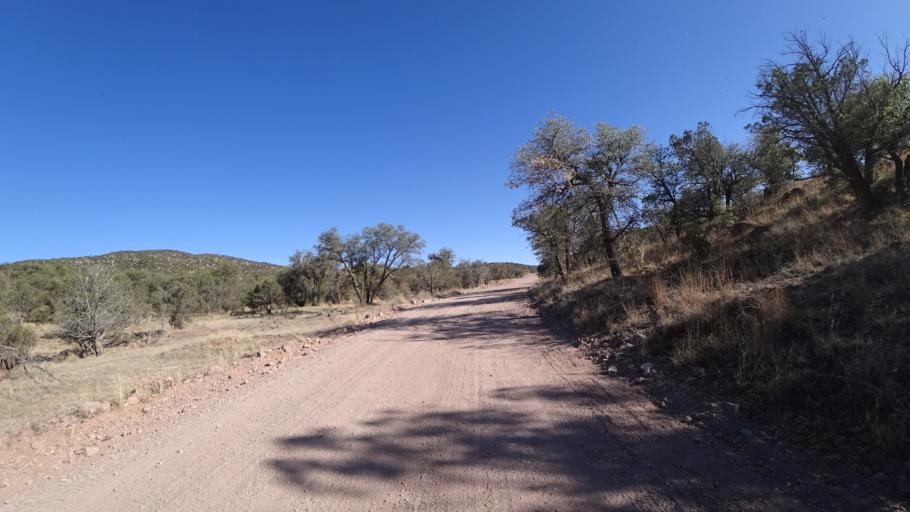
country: US
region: Arizona
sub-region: Cochise County
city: Huachuca City
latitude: 31.5100
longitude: -110.5576
